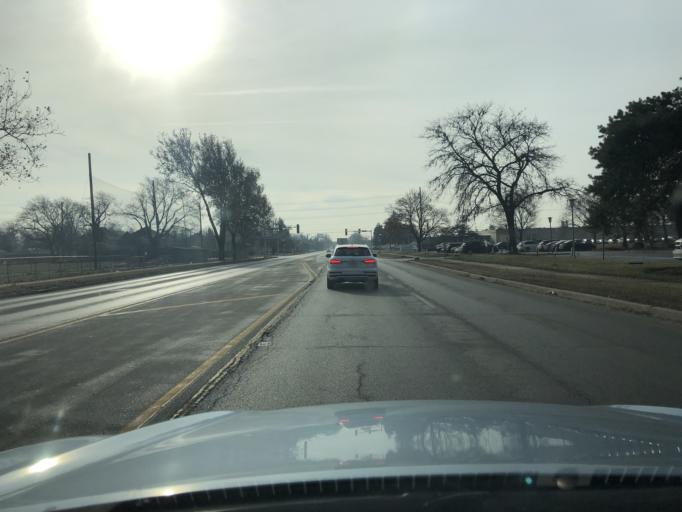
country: US
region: Illinois
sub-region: Cook County
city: Des Plaines
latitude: 42.0175
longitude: -87.9090
